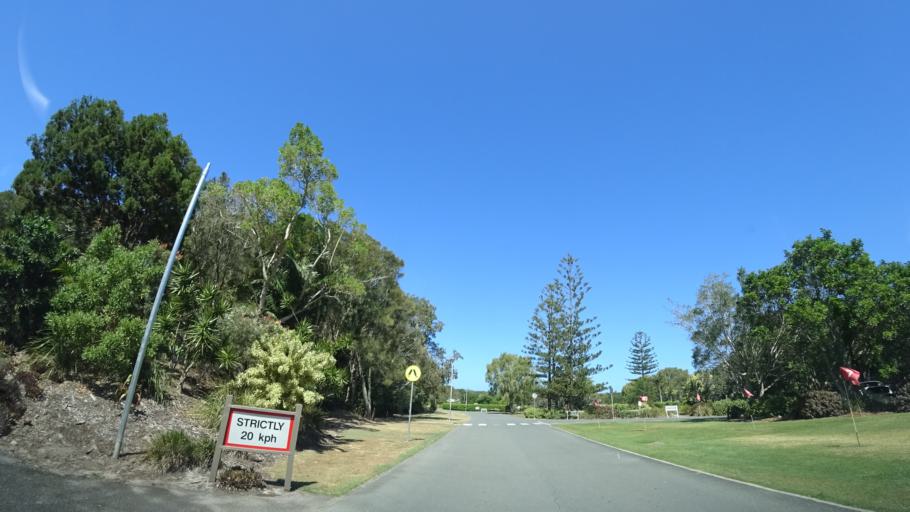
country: AU
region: Queensland
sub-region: Sunshine Coast
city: Mooloolaba
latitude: -26.6311
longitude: 153.0976
